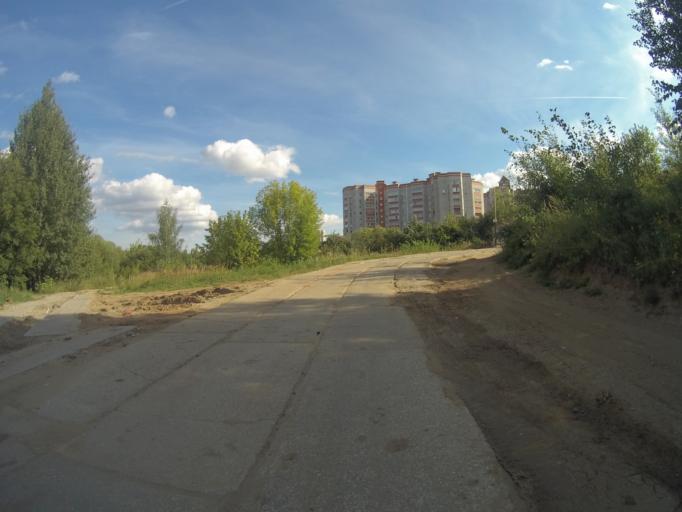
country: RU
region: Vladimir
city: Vladimir
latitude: 56.1387
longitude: 40.3771
